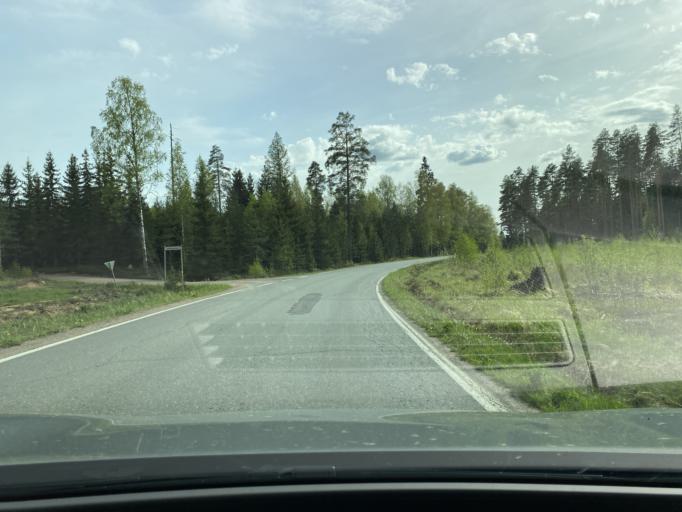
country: FI
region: Varsinais-Suomi
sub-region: Salo
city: Kiikala
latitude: 60.5183
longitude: 23.5381
